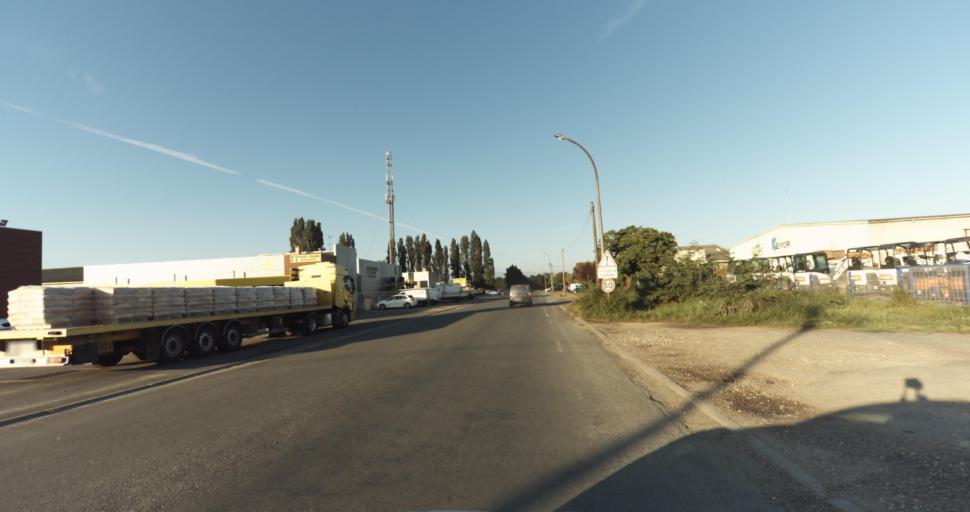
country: FR
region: Aquitaine
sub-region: Departement de la Gironde
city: Bazas
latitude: 44.4375
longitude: -0.2289
